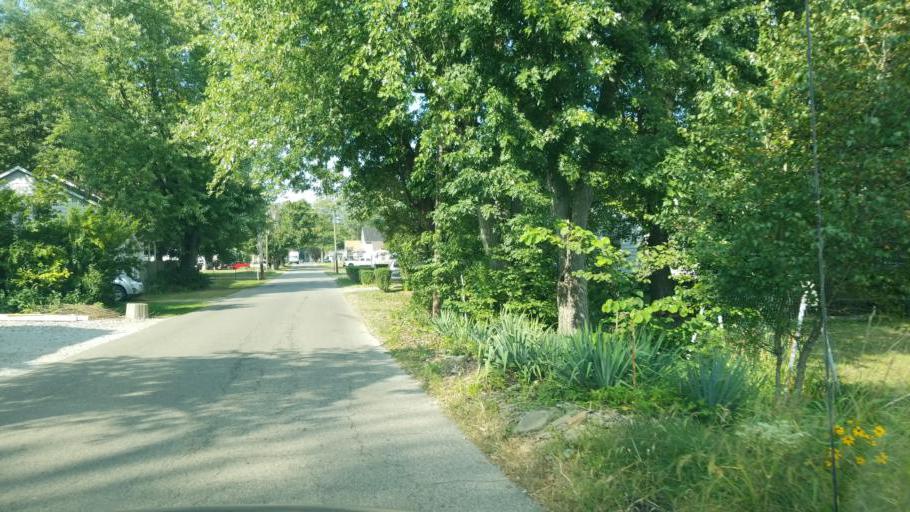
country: US
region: Ohio
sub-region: Knox County
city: Mount Vernon
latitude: 40.3930
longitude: -82.4700
